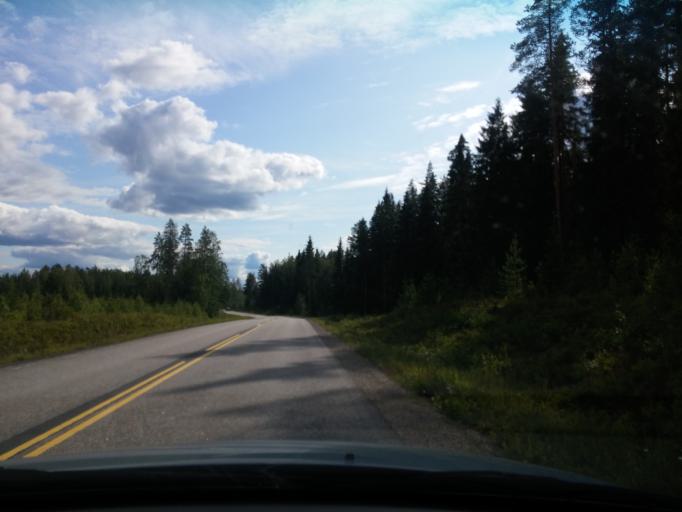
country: FI
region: Central Finland
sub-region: Keuruu
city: Keuruu
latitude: 62.3198
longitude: 24.7310
